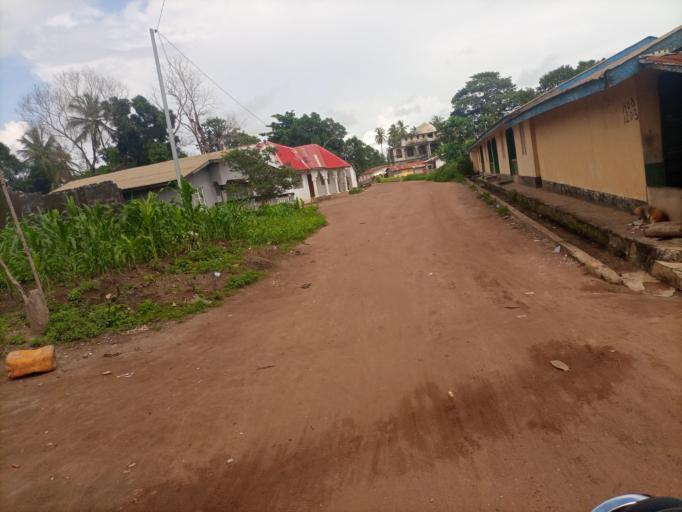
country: SL
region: Northern Province
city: Tintafor
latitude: 8.6318
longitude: -13.2172
